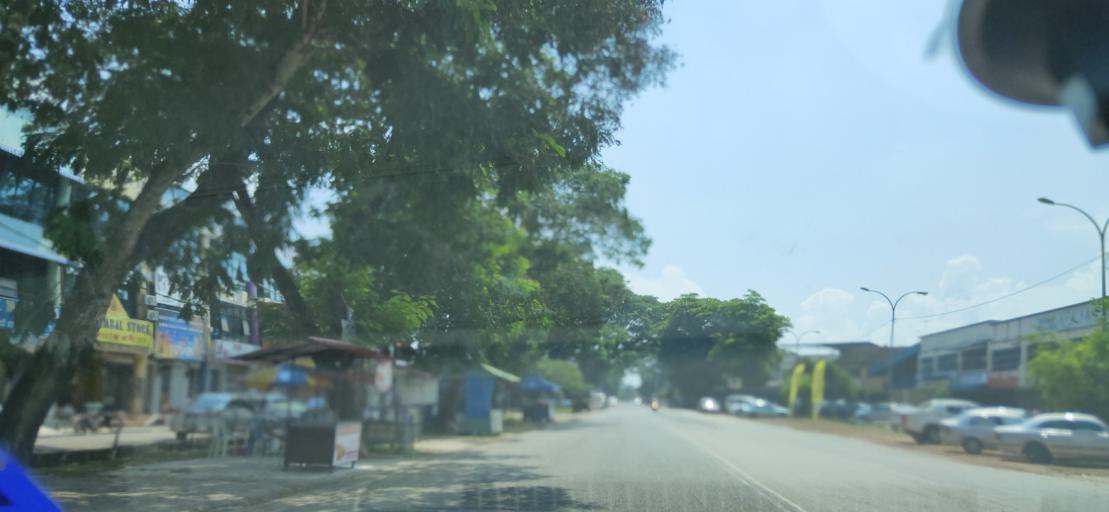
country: MY
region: Kedah
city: Sungai Petani
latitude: 5.6402
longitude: 100.4938
